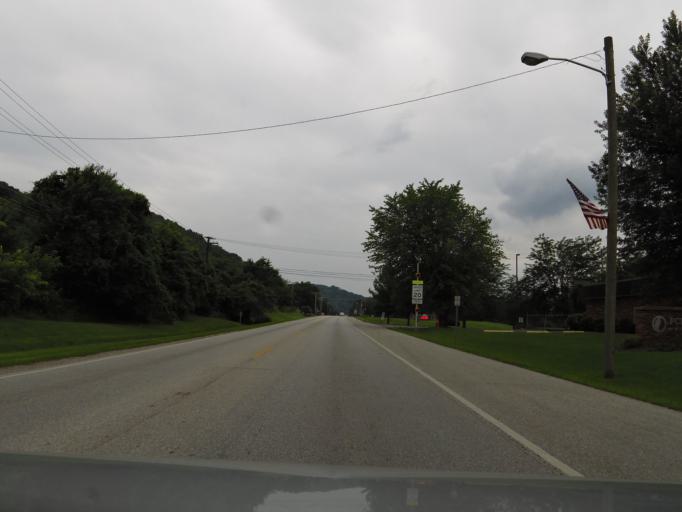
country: US
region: Ohio
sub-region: Brown County
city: Ripley
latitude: 38.7262
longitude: -83.8318
